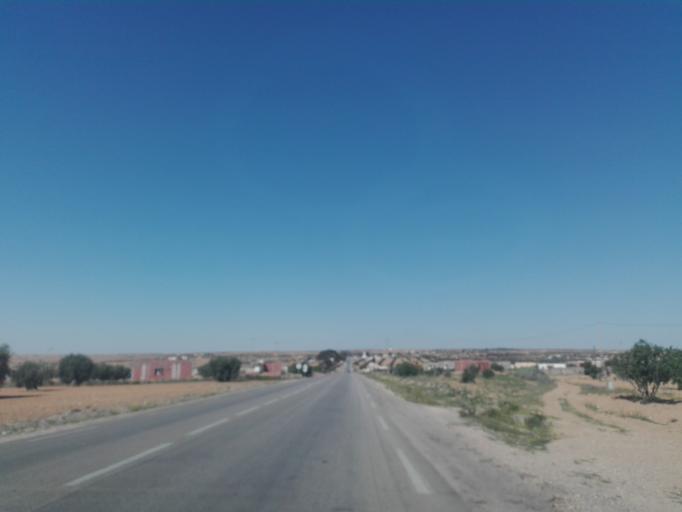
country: TN
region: Safaqis
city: Bi'r `Ali Bin Khalifah
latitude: 34.7410
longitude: 10.3861
